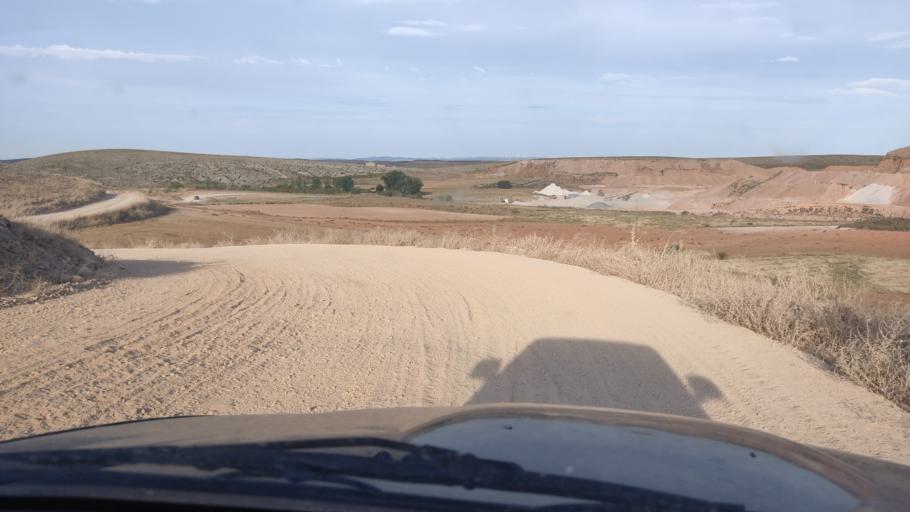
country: ES
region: Aragon
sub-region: Provincia de Teruel
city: Monforte de Moyuela
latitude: 41.0437
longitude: -0.9844
